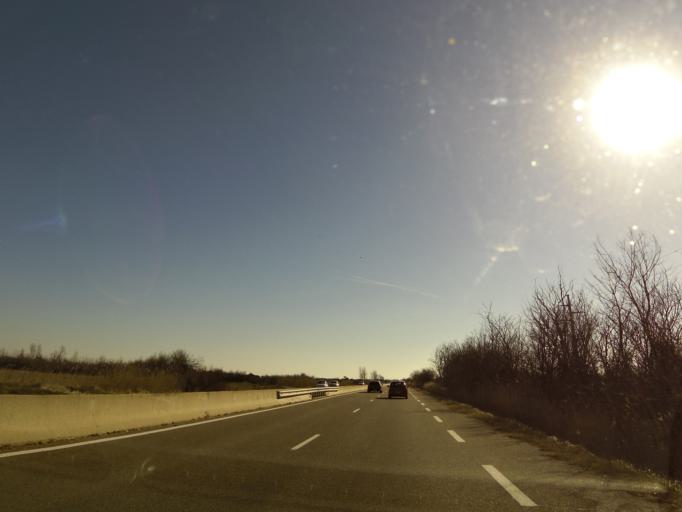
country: FR
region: Languedoc-Roussillon
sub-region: Departement du Gard
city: Aigues-Mortes
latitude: 43.6110
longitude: 4.1929
